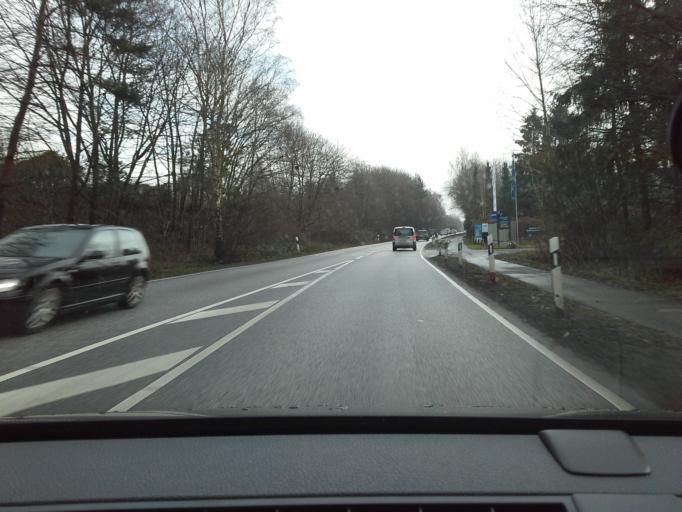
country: DE
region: Schleswig-Holstein
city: Ellerau
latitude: 53.7427
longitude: 9.9548
